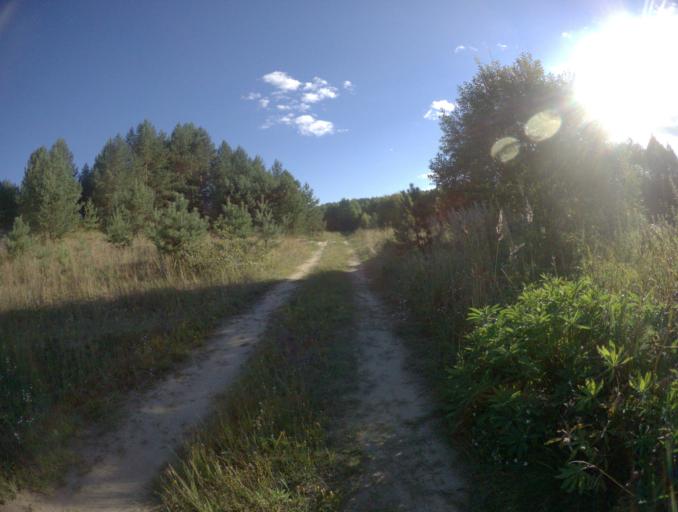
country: RU
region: Vladimir
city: Krasnaya Gorbatka
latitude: 55.7862
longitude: 41.6552
